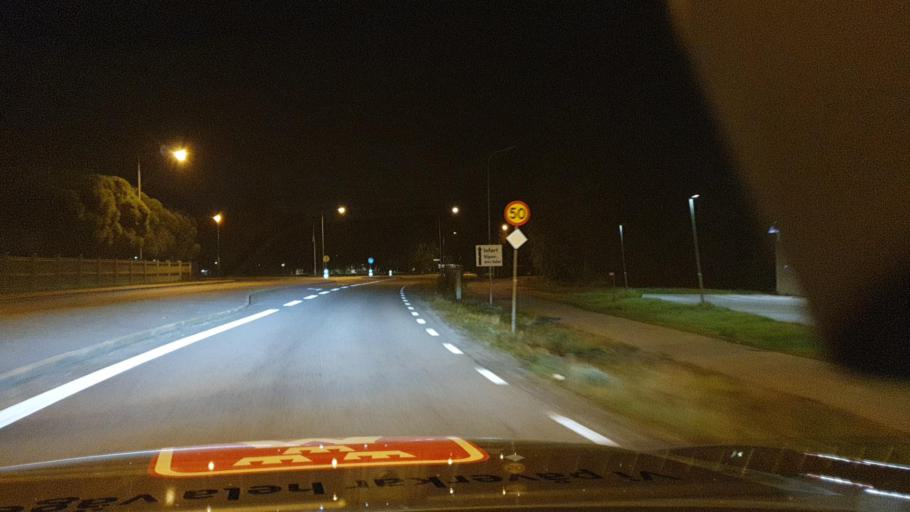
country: SE
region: Vaesternorrland
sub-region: Solleftea Kommun
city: Solleftea
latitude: 63.1775
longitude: 17.2751
